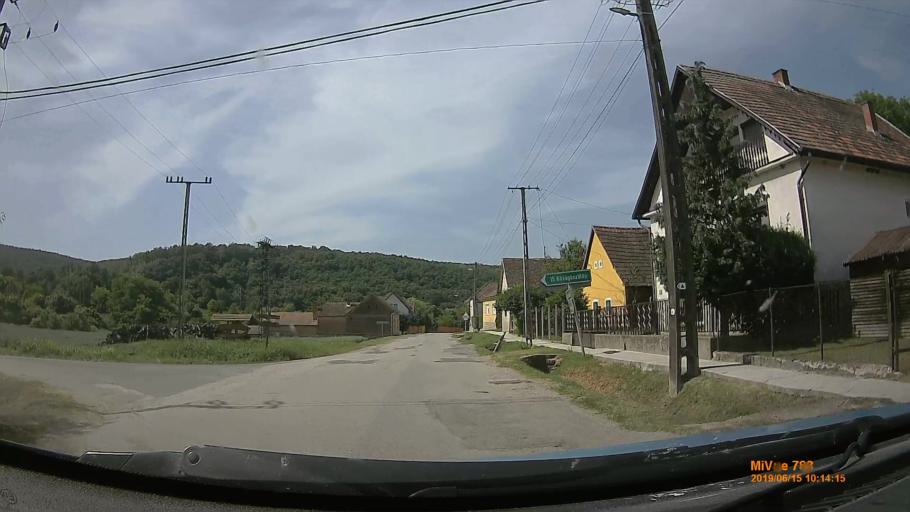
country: HU
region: Baranya
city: Buekkoesd
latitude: 46.1286
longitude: 18.0427
